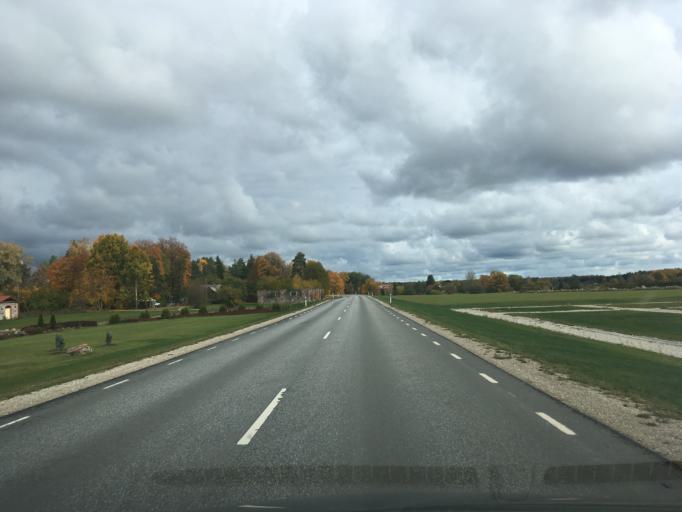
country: EE
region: Harju
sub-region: Anija vald
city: Kehra
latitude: 59.2794
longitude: 25.3701
